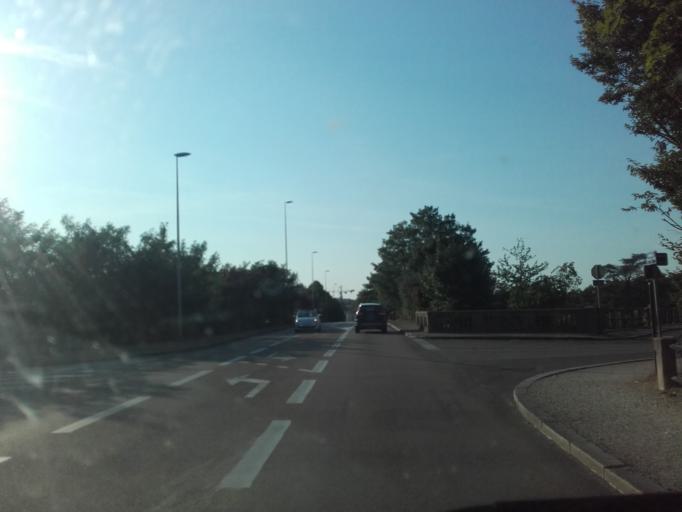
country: FR
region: Bourgogne
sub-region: Departement de l'Yonne
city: Auxerre
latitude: 47.7943
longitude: 3.5855
